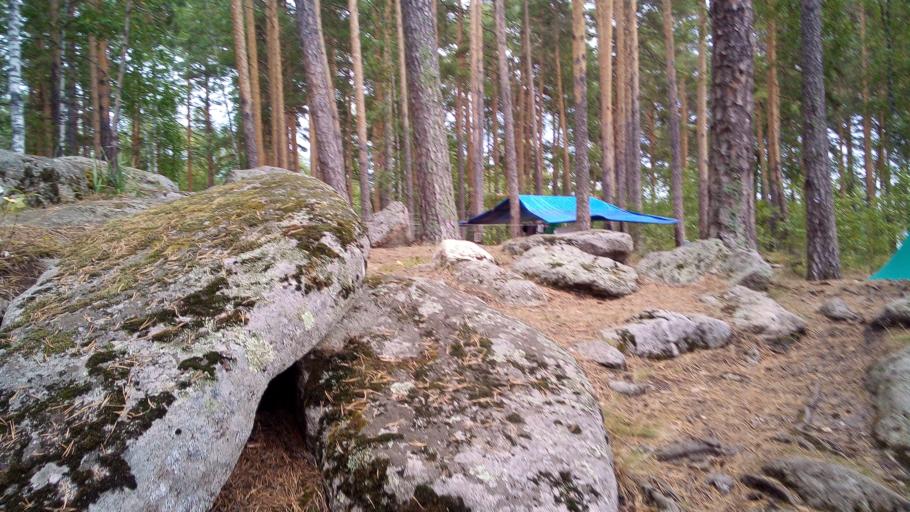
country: RU
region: Chelyabinsk
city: Turgoyak
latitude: 55.1775
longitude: 60.0279
